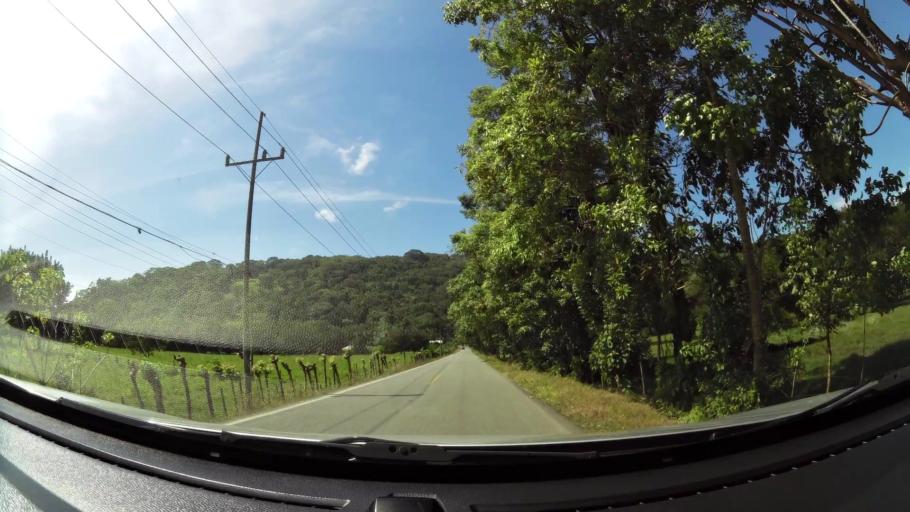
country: CR
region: San Jose
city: San Isidro
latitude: 9.2808
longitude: -83.8570
